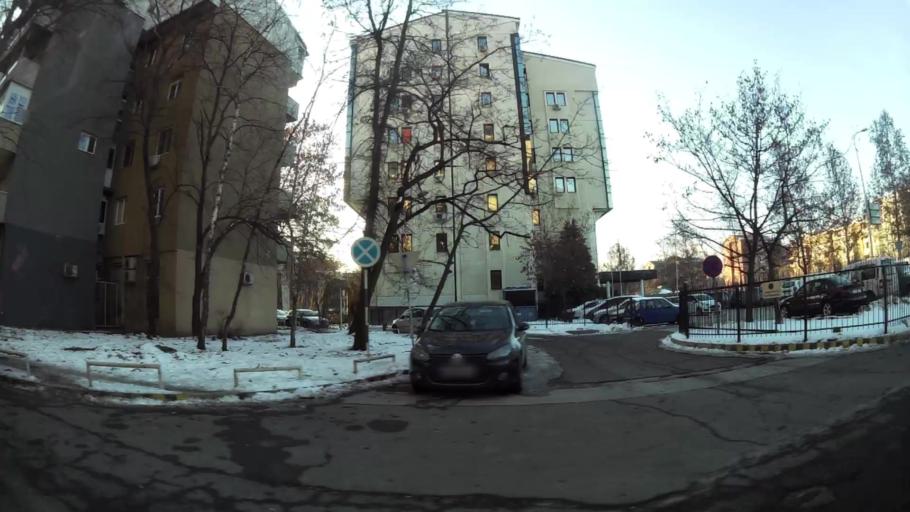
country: MK
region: Karpos
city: Skopje
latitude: 41.9946
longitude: 21.4114
